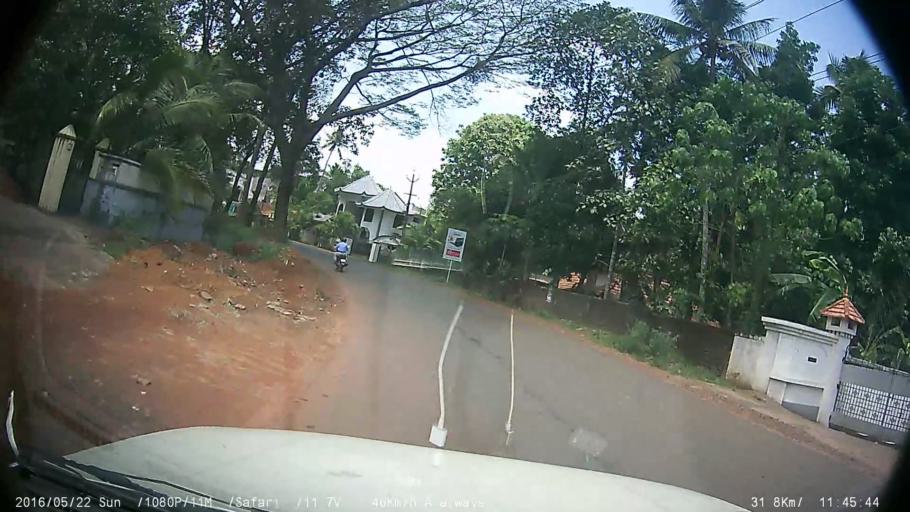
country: IN
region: Kerala
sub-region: Kottayam
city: Kottayam
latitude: 9.5380
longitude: 76.5208
